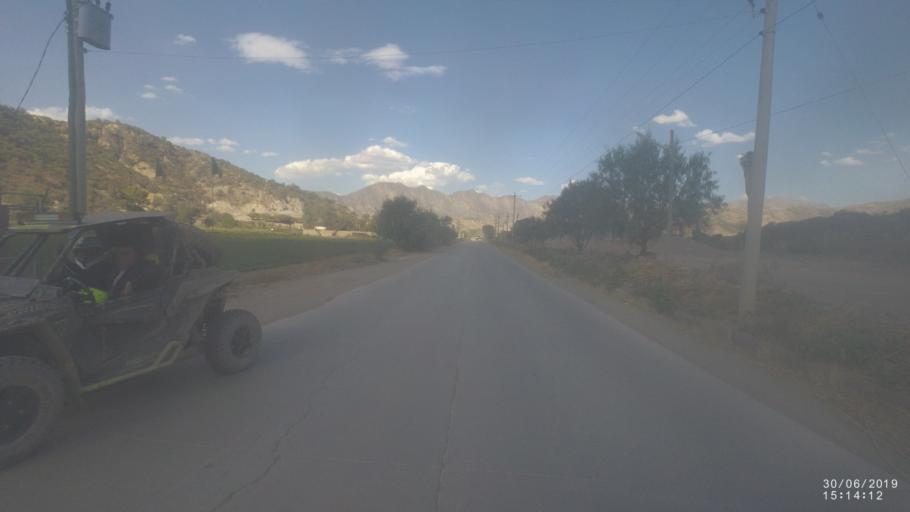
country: BO
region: Cochabamba
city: Irpa Irpa
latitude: -17.7238
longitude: -66.2773
